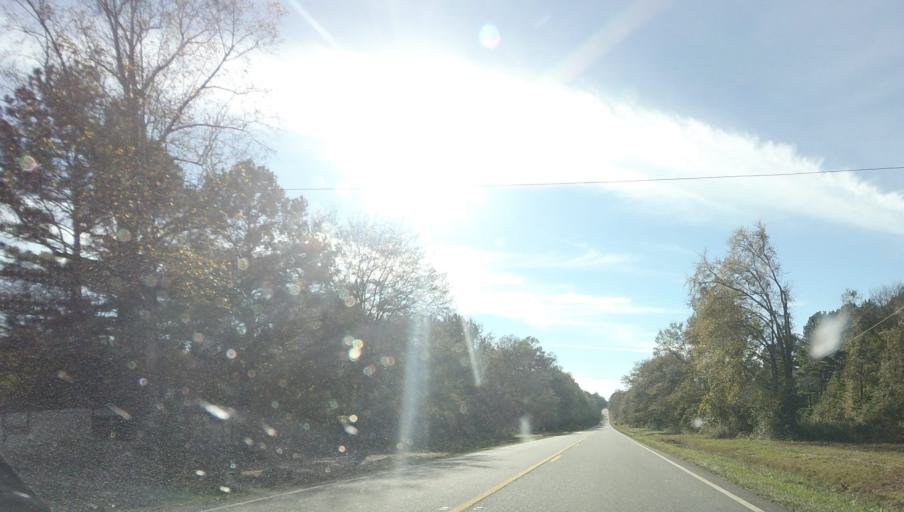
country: US
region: Georgia
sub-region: Talbot County
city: Talbotton
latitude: 32.6942
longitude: -84.4577
